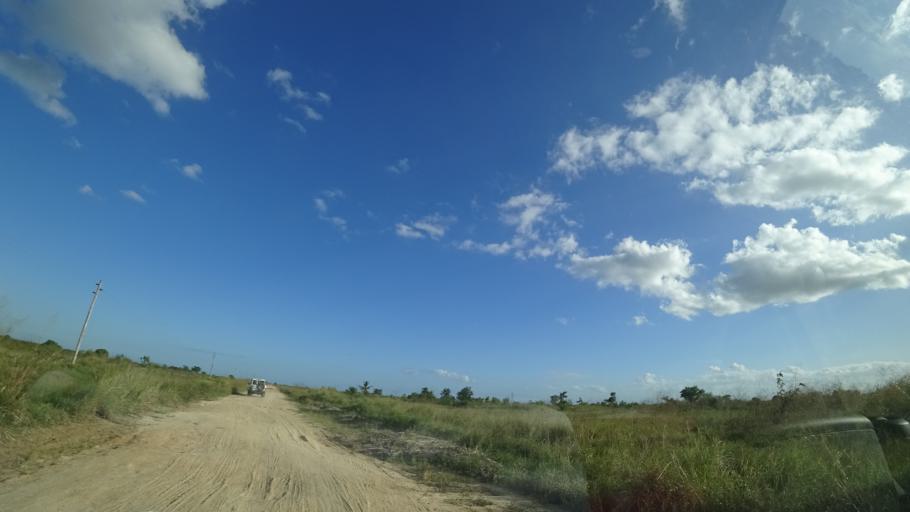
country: MZ
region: Sofala
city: Dondo
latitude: -19.4485
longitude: 34.5623
